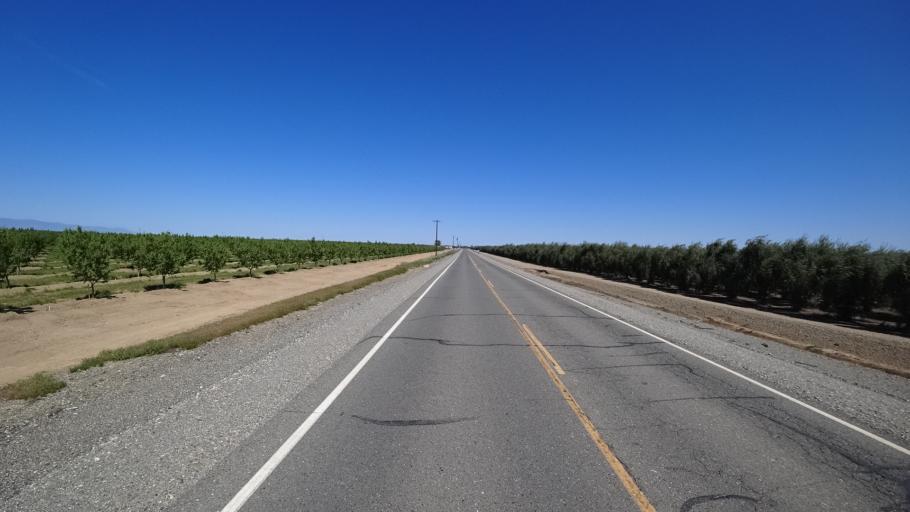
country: US
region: California
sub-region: Glenn County
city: Orland
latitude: 39.6819
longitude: -122.1404
